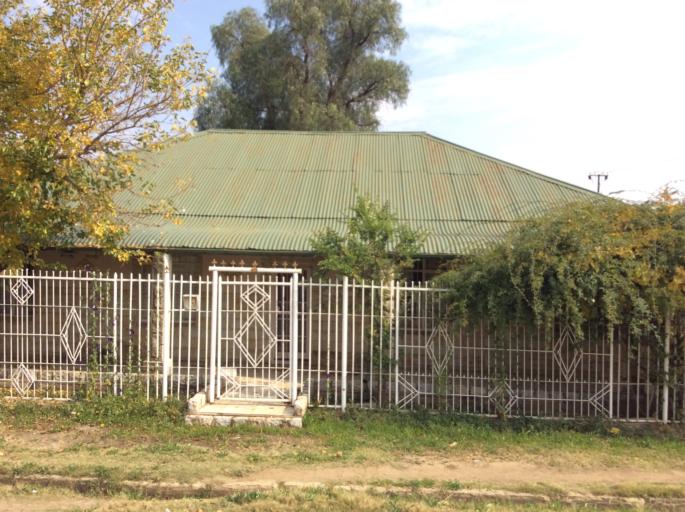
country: LS
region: Mafeteng
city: Mafeteng
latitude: -29.7285
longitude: 27.0367
